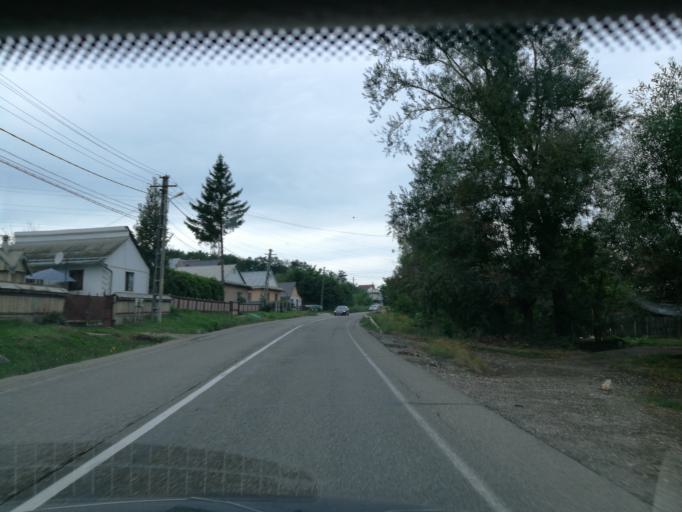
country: RO
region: Suceava
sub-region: Comuna Bunesti
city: Bunesti
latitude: 47.5263
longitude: 26.2804
